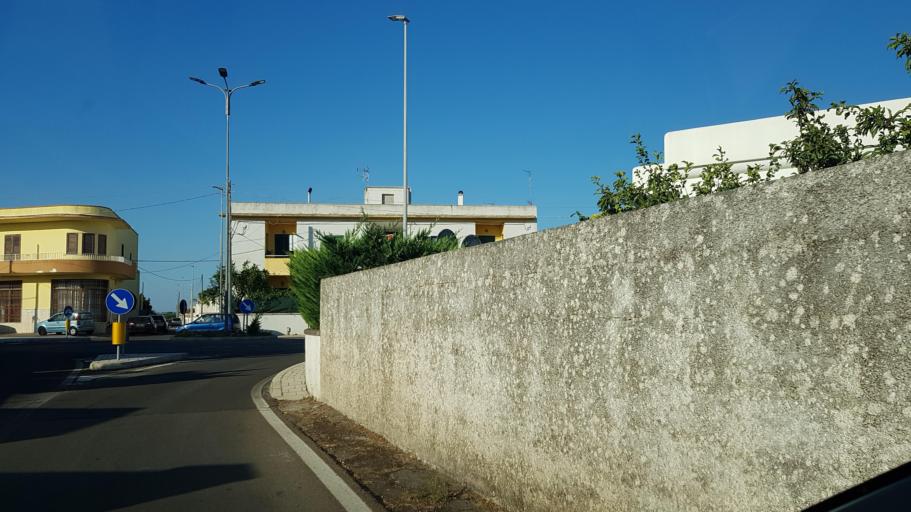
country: IT
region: Apulia
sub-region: Provincia di Lecce
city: Marittima
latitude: 39.9993
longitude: 18.3948
